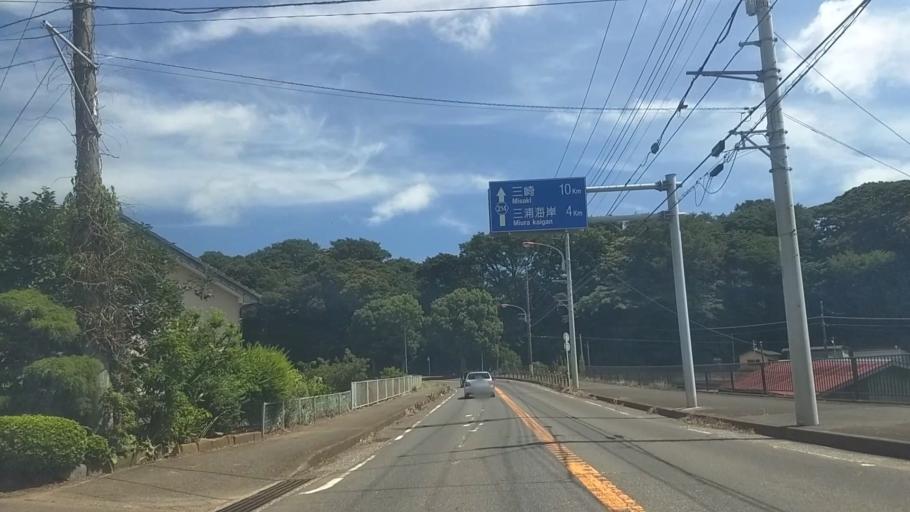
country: JP
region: Kanagawa
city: Miura
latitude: 35.2084
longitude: 139.6444
